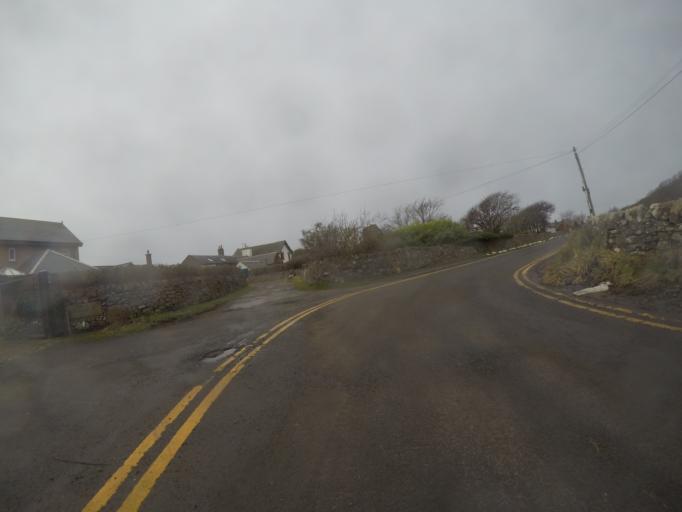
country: GB
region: Scotland
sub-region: North Ayrshire
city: West Kilbride
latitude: 55.6987
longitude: -4.9033
